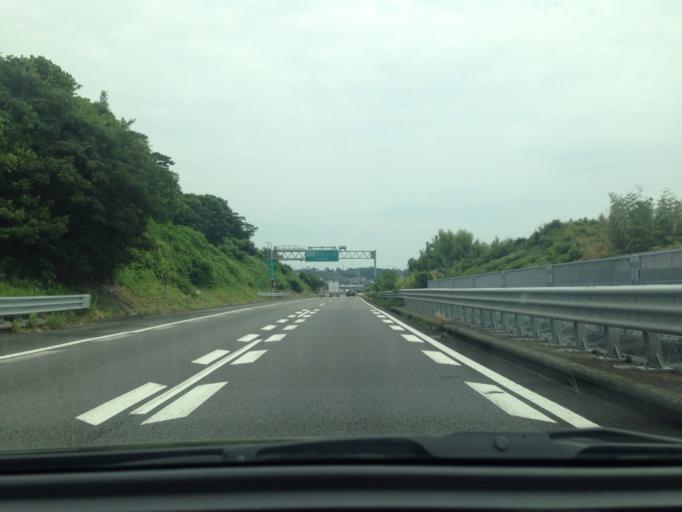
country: JP
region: Shizuoka
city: Shimada
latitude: 34.7701
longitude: 138.2209
